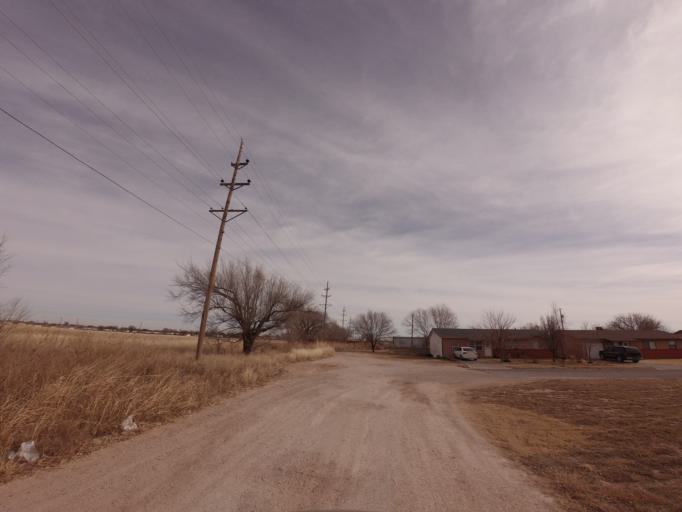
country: US
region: New Mexico
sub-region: Curry County
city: Clovis
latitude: 34.4119
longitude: -103.2355
